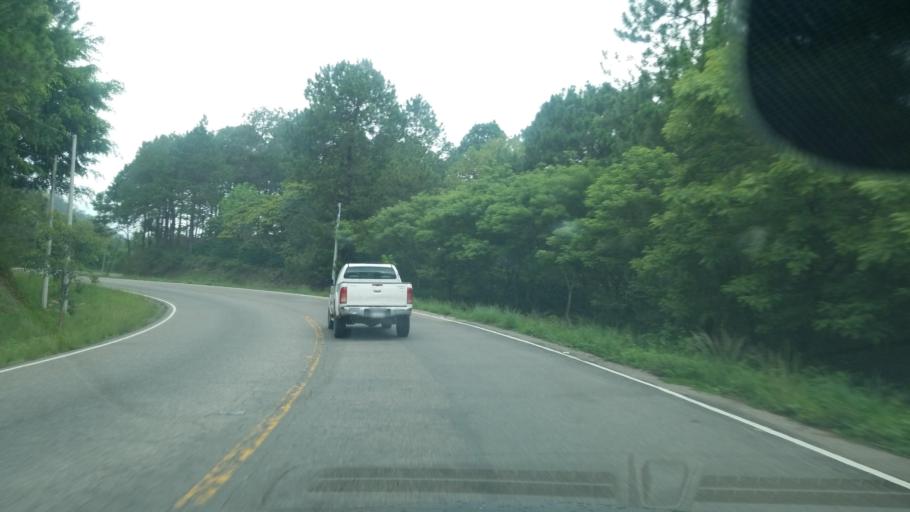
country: HN
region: Ocotepeque
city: Sinuapa
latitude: 14.4601
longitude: -89.1561
